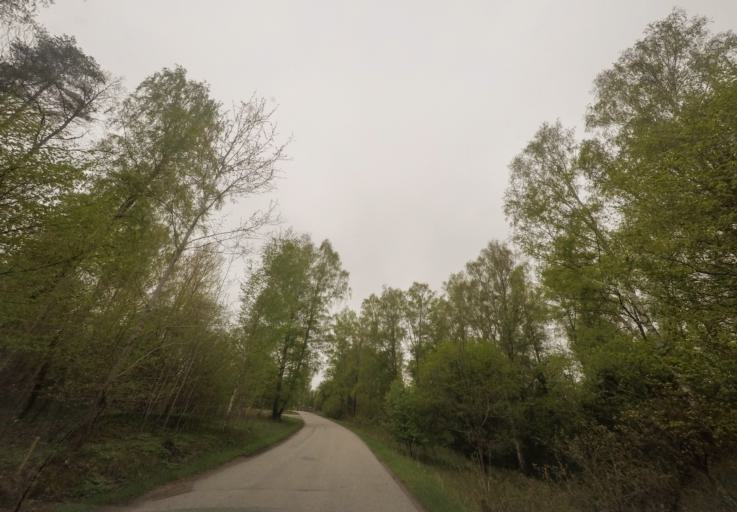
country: SE
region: Vaestmanland
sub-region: Vasteras
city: Vasteras
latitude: 59.5744
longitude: 16.6130
